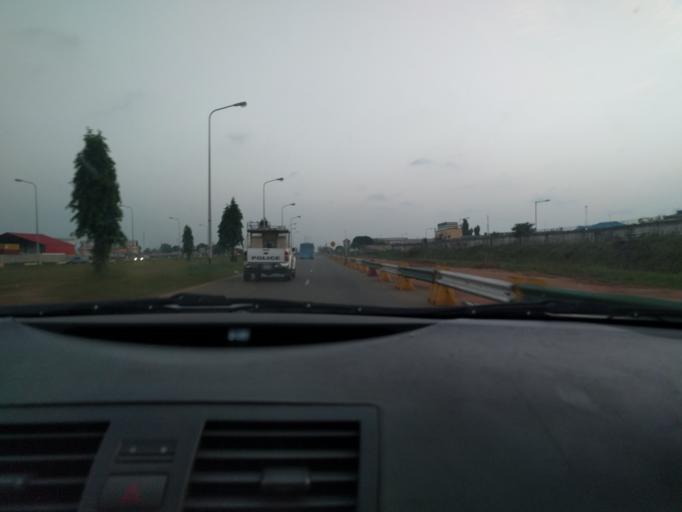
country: NG
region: Lagos
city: Oshodi
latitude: 6.5689
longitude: 3.3211
